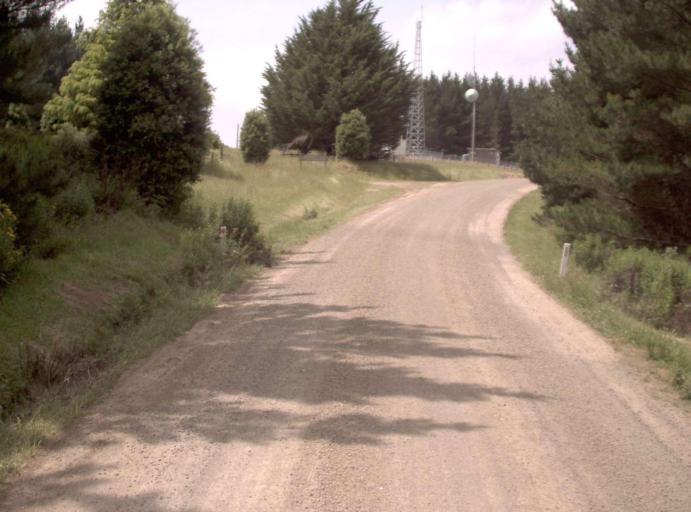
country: AU
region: Victoria
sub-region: Latrobe
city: Traralgon
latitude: -38.4070
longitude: 146.6375
